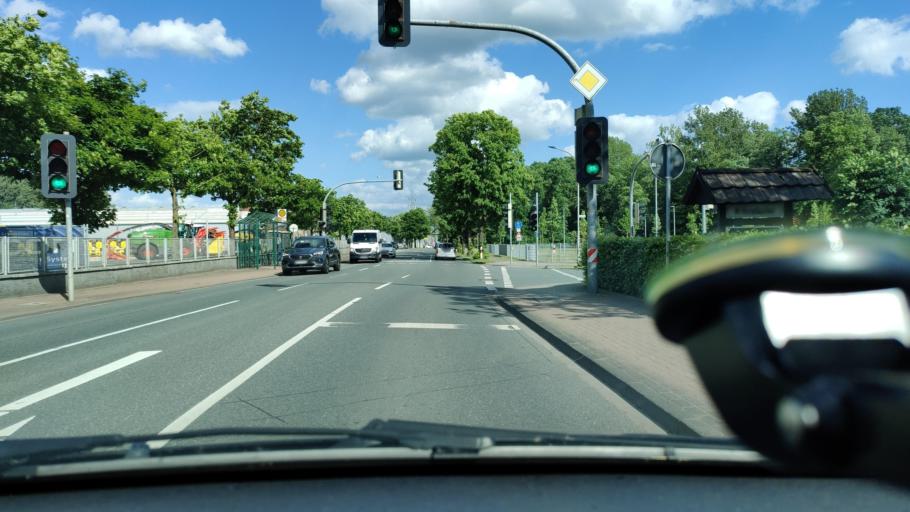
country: DE
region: North Rhine-Westphalia
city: Stadtlohn
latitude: 51.9918
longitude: 6.9305
